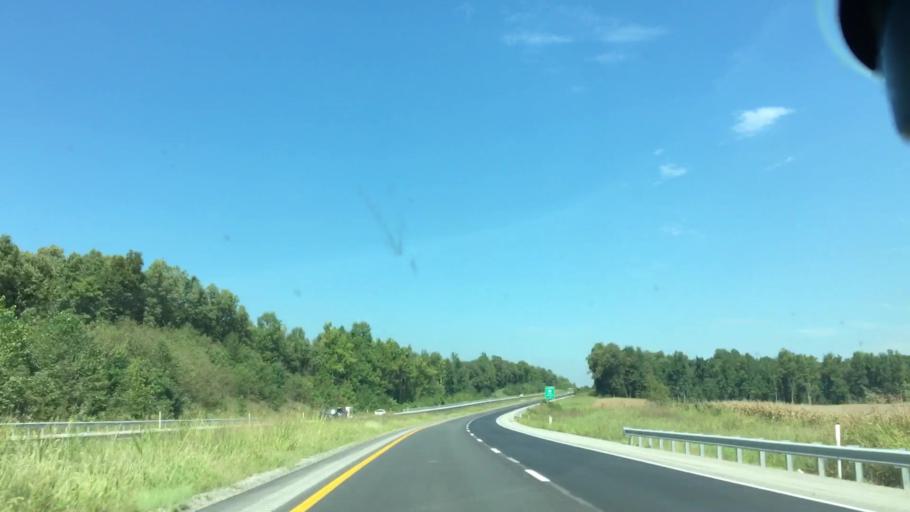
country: US
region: Kentucky
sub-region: Hopkins County
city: Madisonville
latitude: 37.4637
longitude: -87.4804
